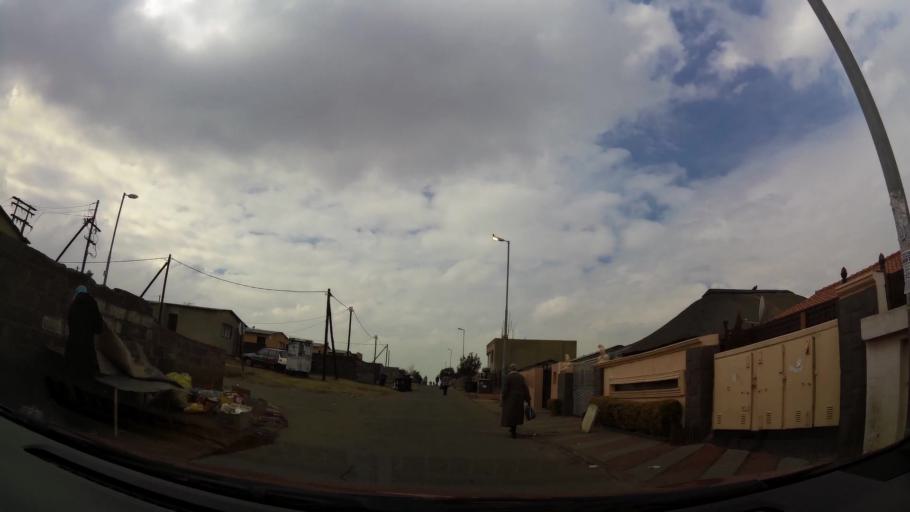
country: ZA
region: Gauteng
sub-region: City of Johannesburg Metropolitan Municipality
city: Soweto
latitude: -26.2556
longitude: 27.8229
